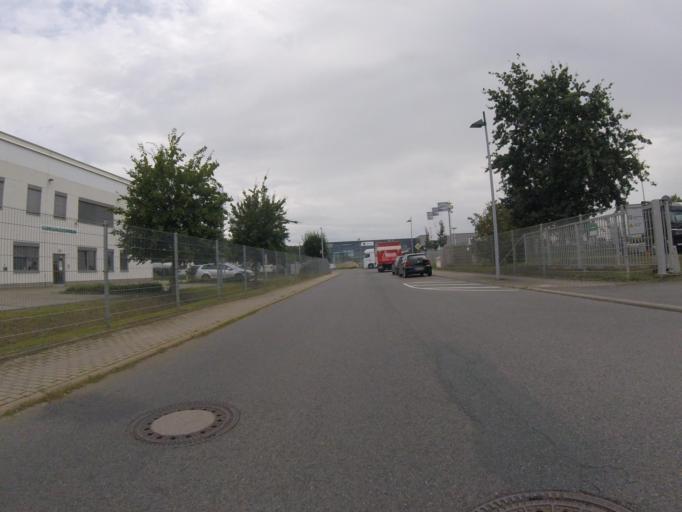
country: DE
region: Brandenburg
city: Wildau
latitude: 52.3202
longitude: 13.5957
